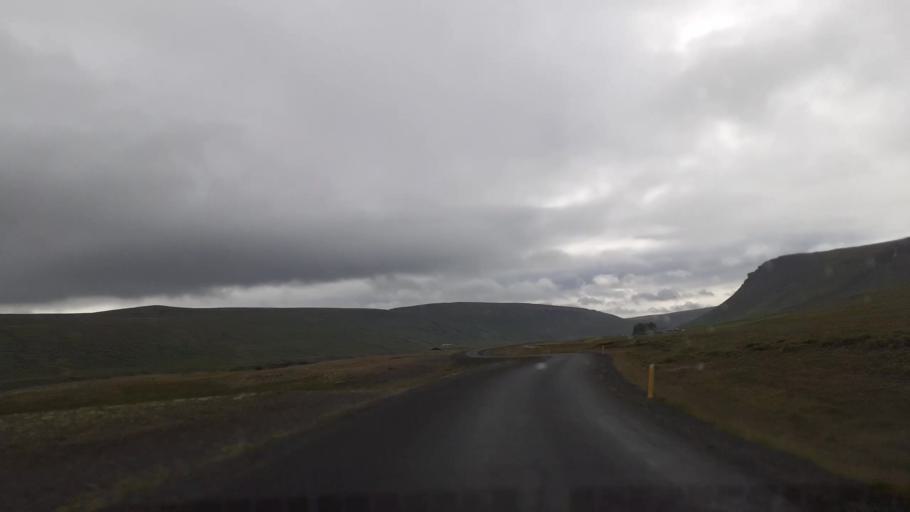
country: IS
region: East
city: Egilsstadir
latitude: 65.6222
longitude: -15.0849
